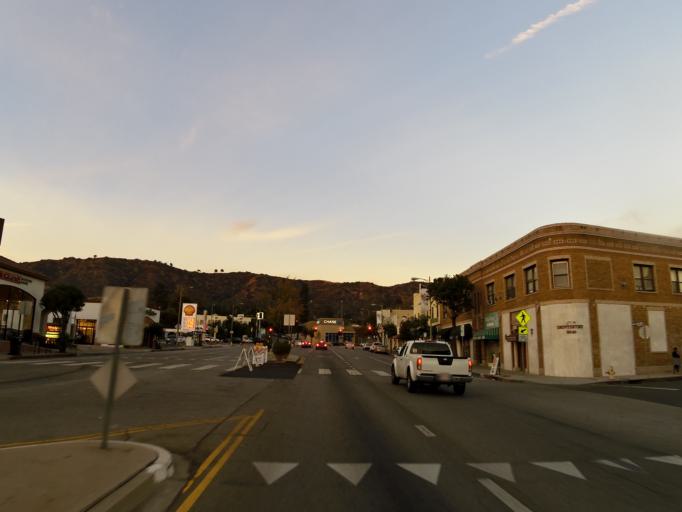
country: US
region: California
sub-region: Los Angeles County
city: Glendale
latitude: 34.1379
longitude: -118.2144
